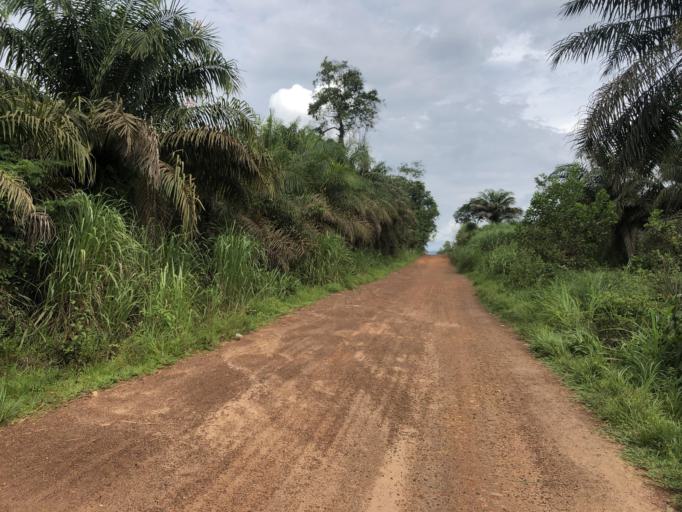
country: SL
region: Northern Province
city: Masaka
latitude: 8.7509
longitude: -11.8440
